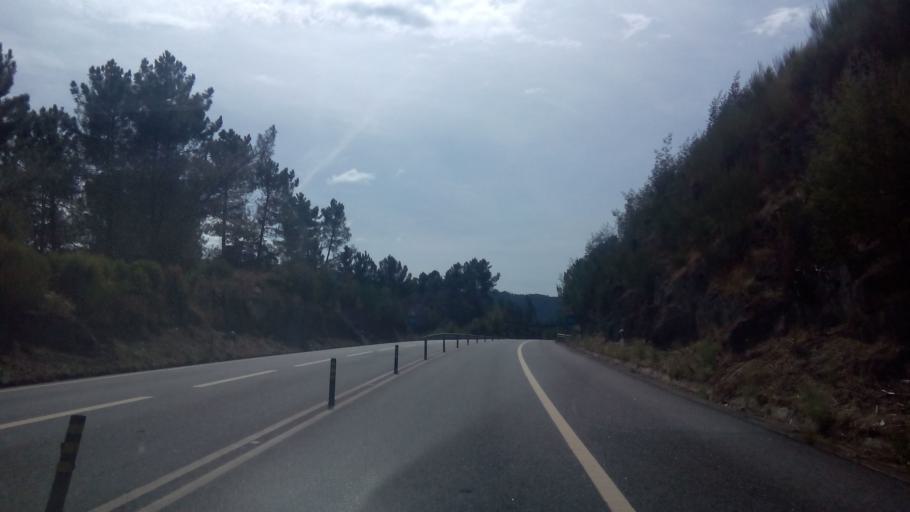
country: PT
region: Porto
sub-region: Amarante
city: Amarante
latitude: 41.2682
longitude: -8.0172
